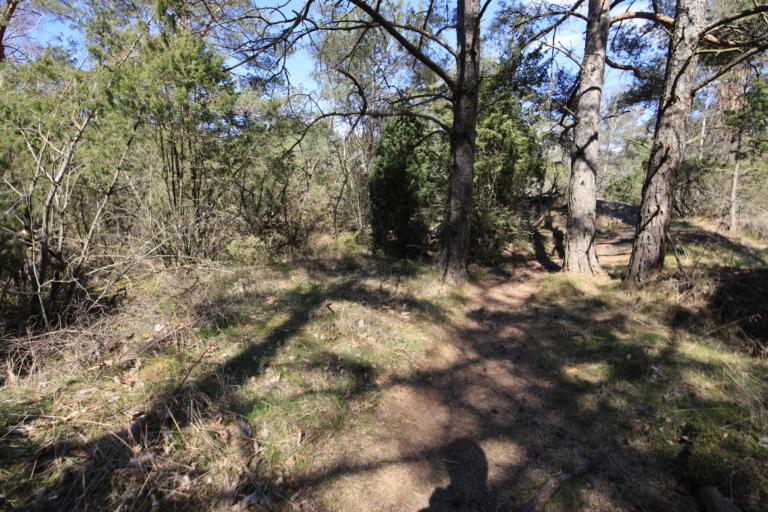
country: SE
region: Halland
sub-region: Varbergs Kommun
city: Varberg
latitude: 57.1764
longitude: 12.2396
